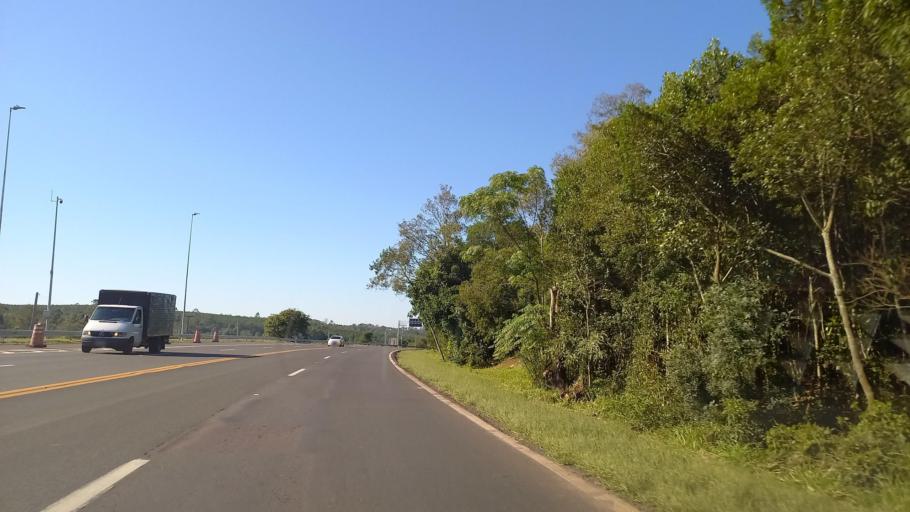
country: BR
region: Rio Grande do Sul
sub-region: Montenegro
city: Montenegro
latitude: -29.7927
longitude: -51.5320
